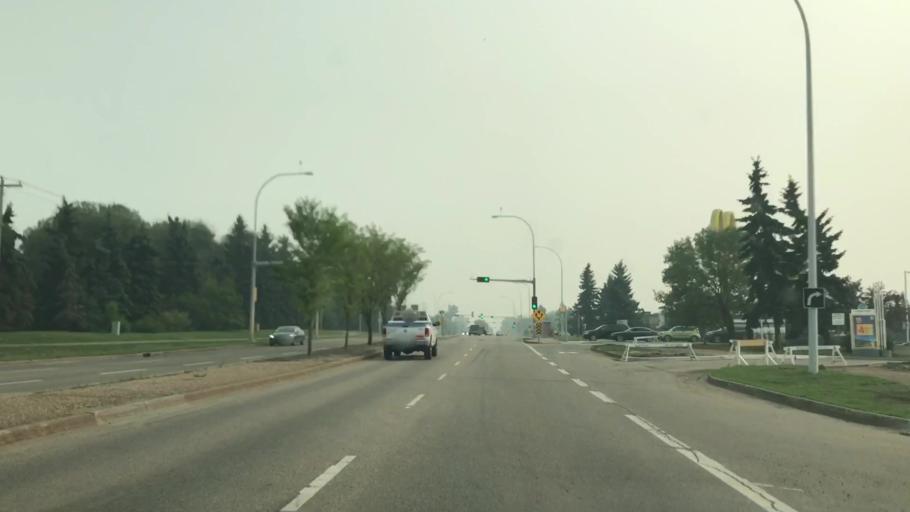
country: CA
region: Alberta
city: Sherwood Park
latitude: 53.5402
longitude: -113.3203
